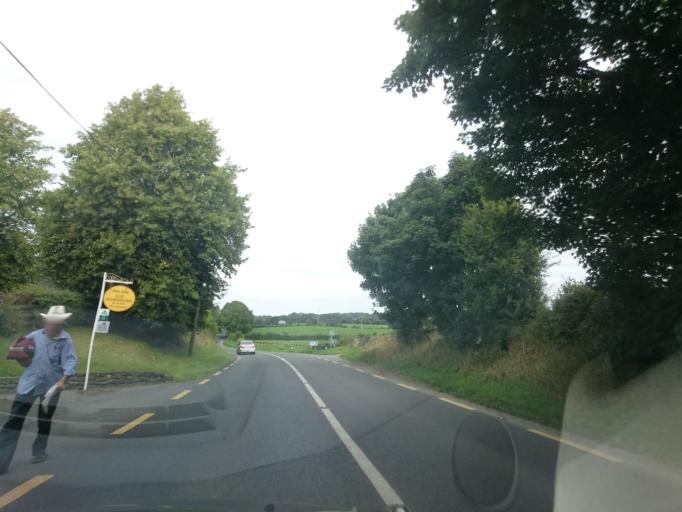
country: IE
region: Leinster
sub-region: Kilkenny
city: Kilkenny
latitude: 52.6837
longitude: -7.2550
